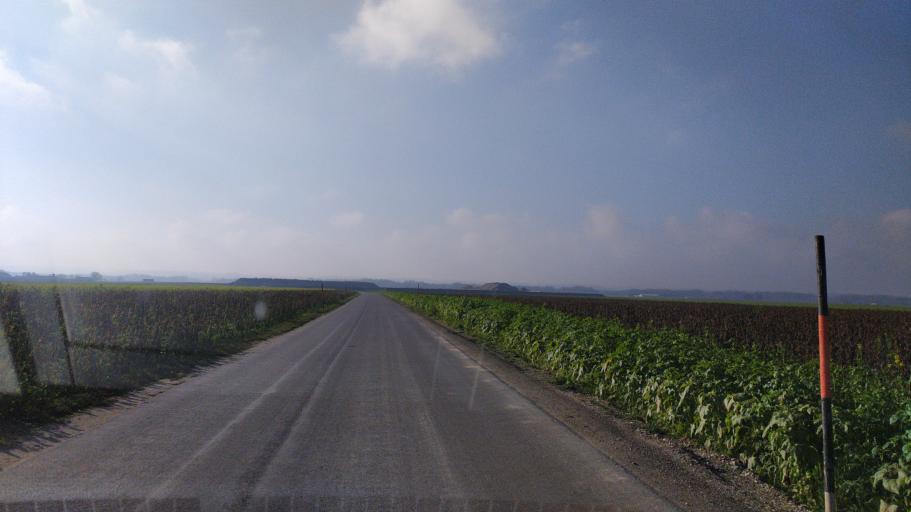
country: AT
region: Upper Austria
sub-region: Politischer Bezirk Perg
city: Perg
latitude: 48.2056
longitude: 14.6529
